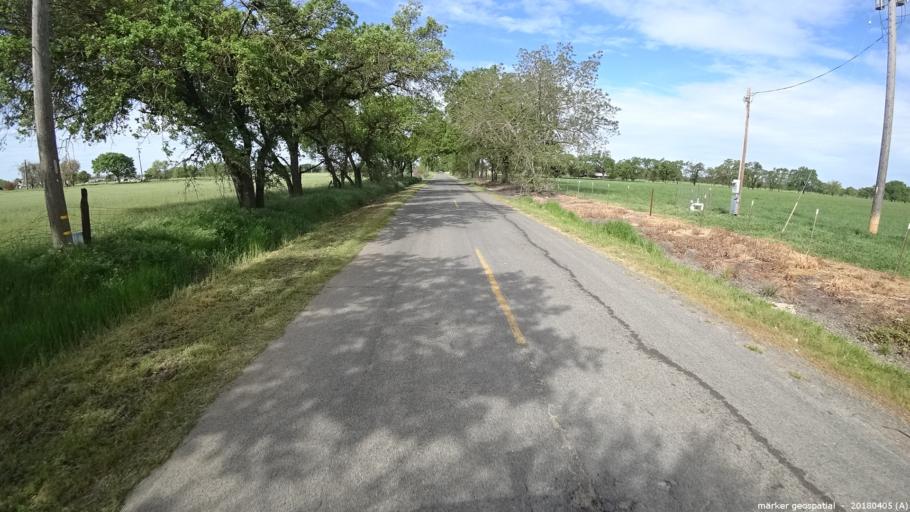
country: US
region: California
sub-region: Sacramento County
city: Galt
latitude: 38.2619
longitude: -121.3402
